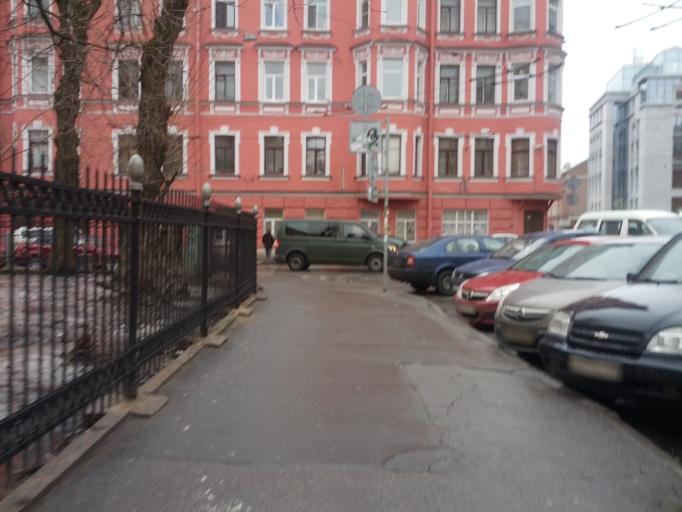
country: RU
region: St.-Petersburg
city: Petrogradka
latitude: 59.9607
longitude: 30.3116
